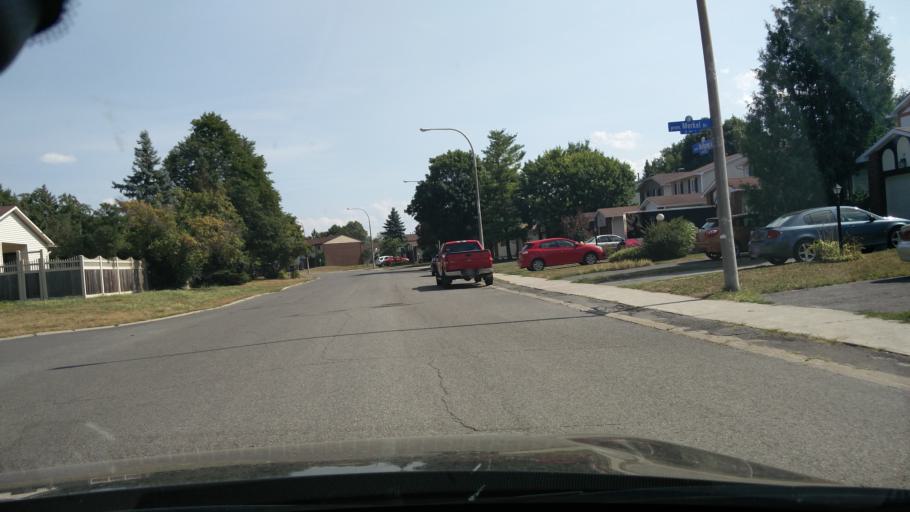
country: CA
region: Ontario
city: Bells Corners
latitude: 45.2890
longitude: -75.7521
